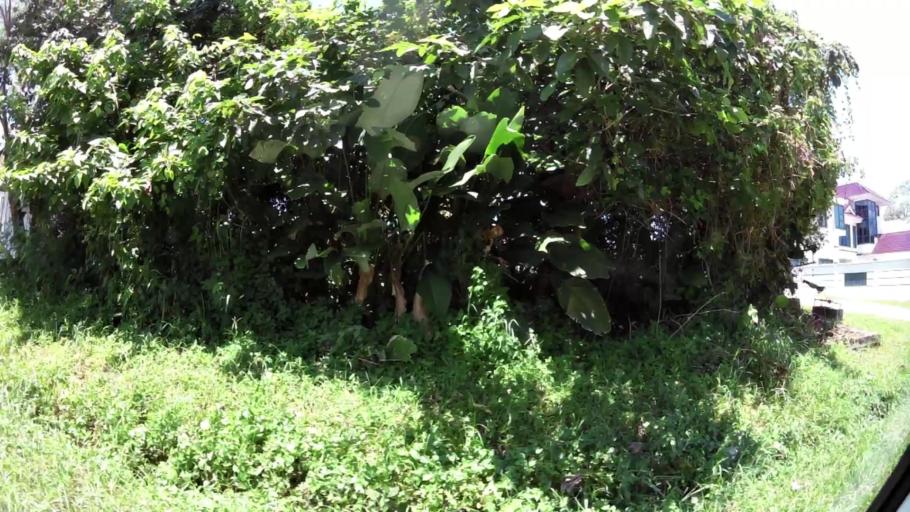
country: BN
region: Brunei and Muara
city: Bandar Seri Begawan
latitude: 4.9425
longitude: 114.9593
